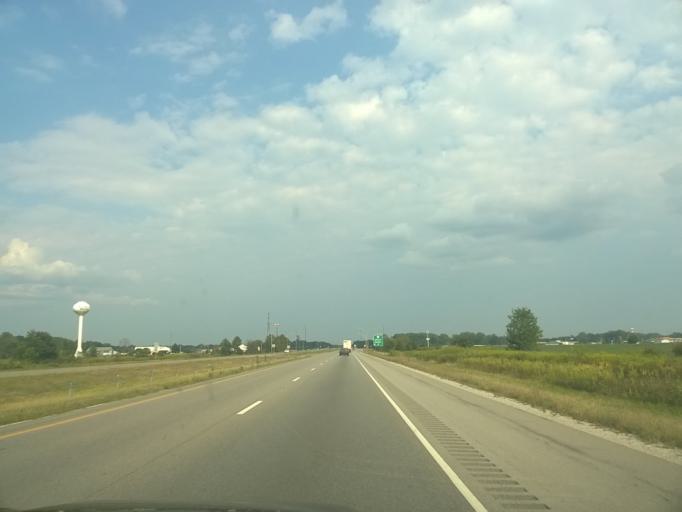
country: US
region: Indiana
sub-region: Clay County
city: Brazil
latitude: 39.4495
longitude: -87.1357
